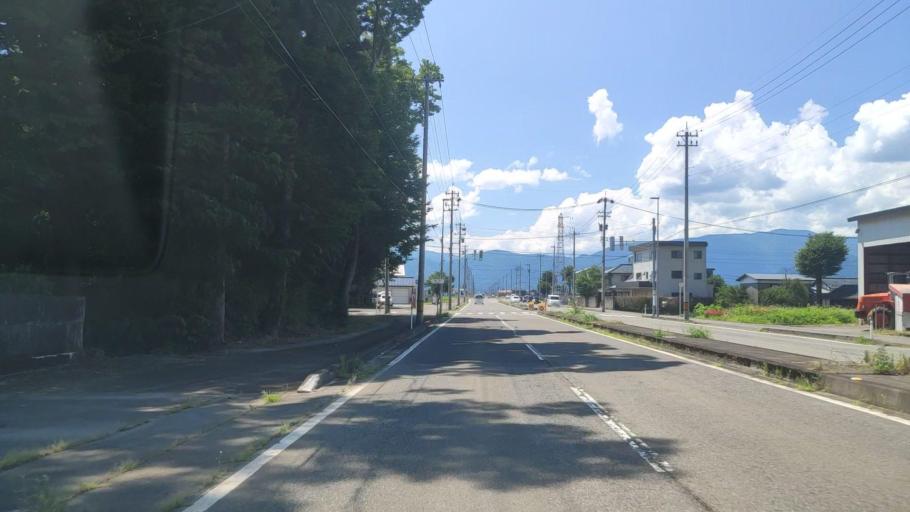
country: JP
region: Fukui
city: Ono
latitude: 35.9963
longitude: 136.5094
